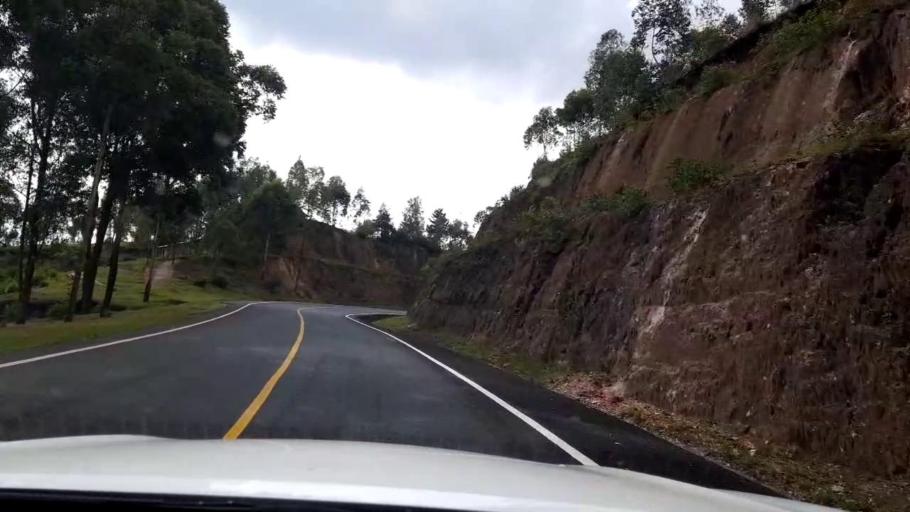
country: RW
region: Southern Province
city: Gitarama
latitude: -2.0290
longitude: 29.7174
